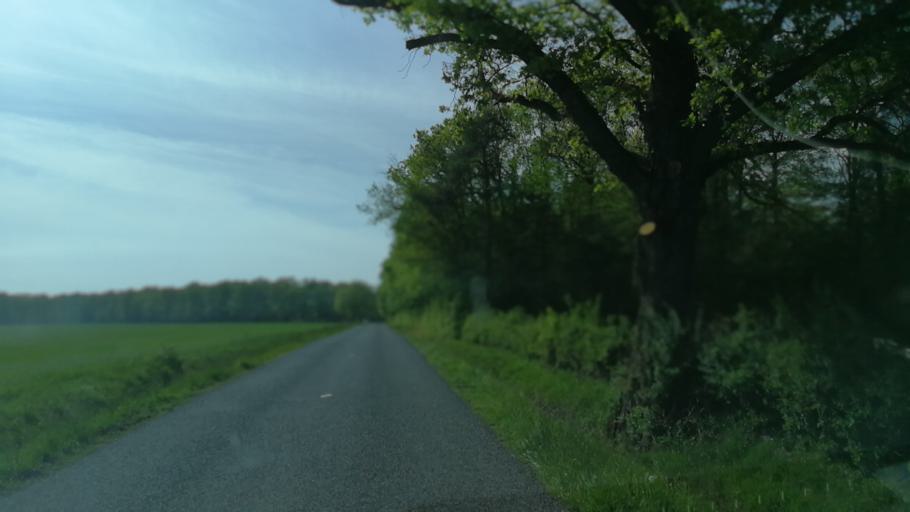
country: FR
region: Auvergne
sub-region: Departement de l'Allier
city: Neuilly-le-Real
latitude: 46.5153
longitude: 3.4479
